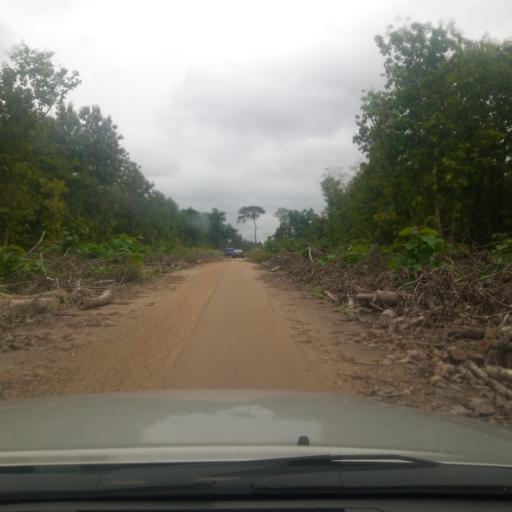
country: NG
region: Ebonyi
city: Effium
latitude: 6.6238
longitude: 8.0476
